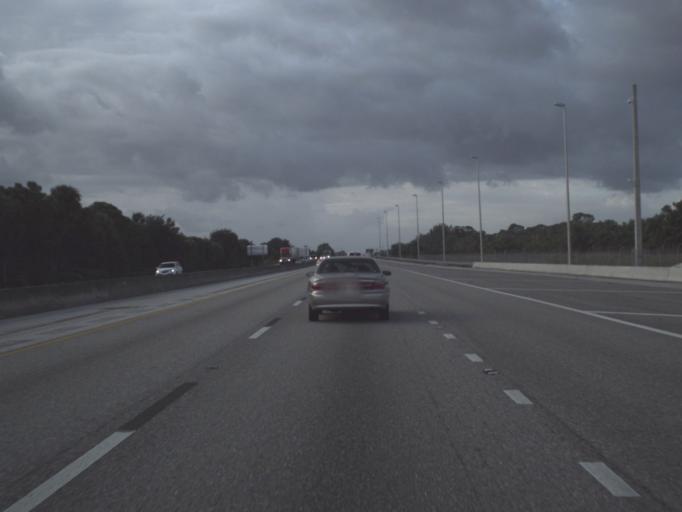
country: US
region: Florida
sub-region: Palm Beach County
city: Greenacres City
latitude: 26.6057
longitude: -80.1737
